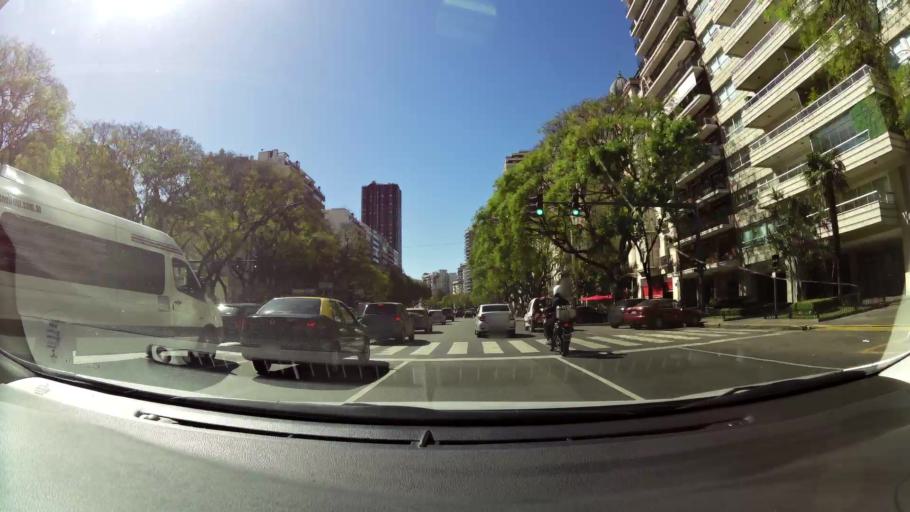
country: AR
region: Buenos Aires F.D.
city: Retiro
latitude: -34.5794
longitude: -58.4060
